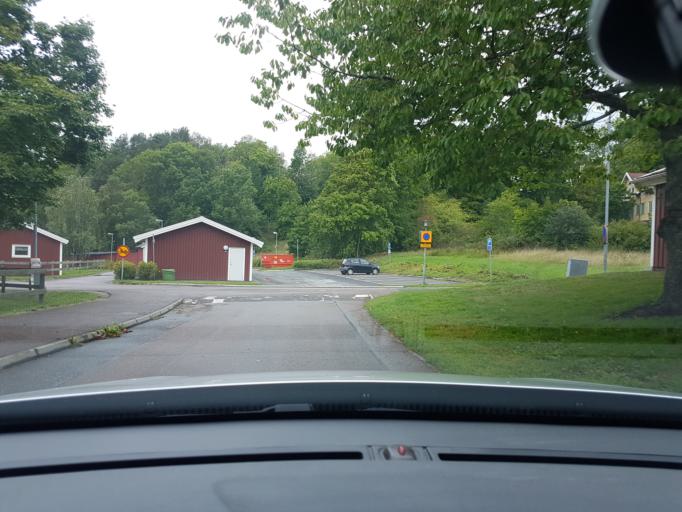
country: SE
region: Vaestra Goetaland
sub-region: Ale Kommun
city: Salanda
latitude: 57.9859
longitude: 12.2167
